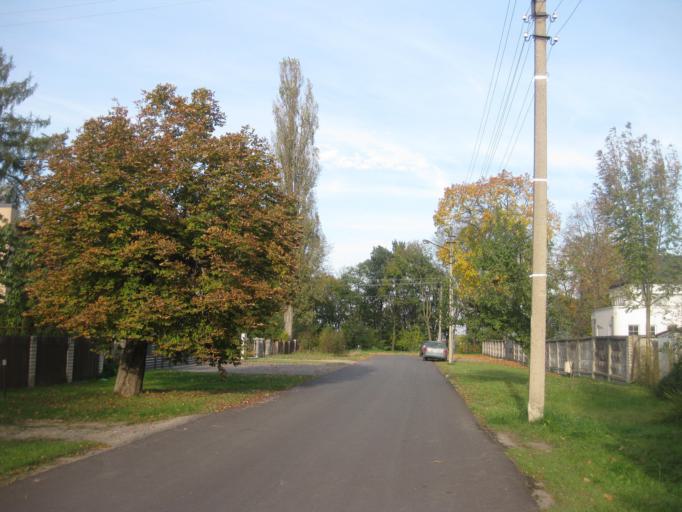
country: LT
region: Kauno apskritis
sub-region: Kaunas
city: Kaunas
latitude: 54.8938
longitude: 23.8735
